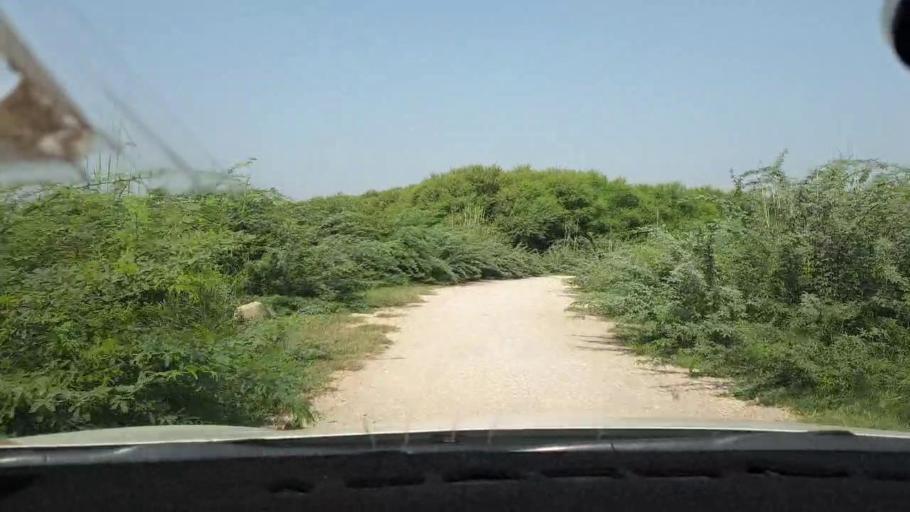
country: PK
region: Sindh
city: Tando Mittha Khan
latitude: 25.9449
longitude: 69.2985
